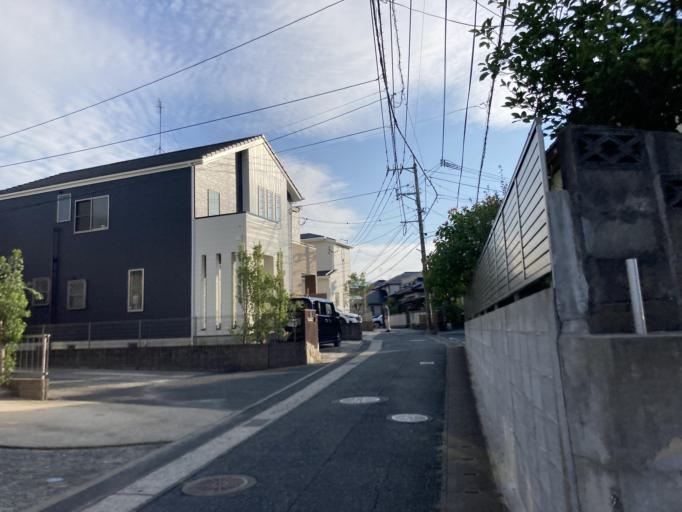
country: JP
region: Fukuoka
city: Fukuoka-shi
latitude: 33.5479
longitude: 130.3544
